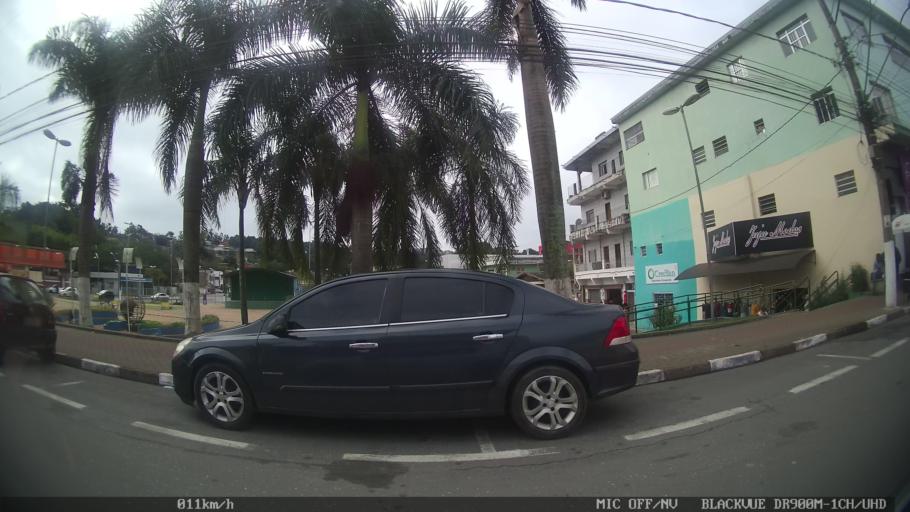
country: BR
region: Sao Paulo
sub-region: Cajati
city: Cajati
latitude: -24.7266
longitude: -48.1117
